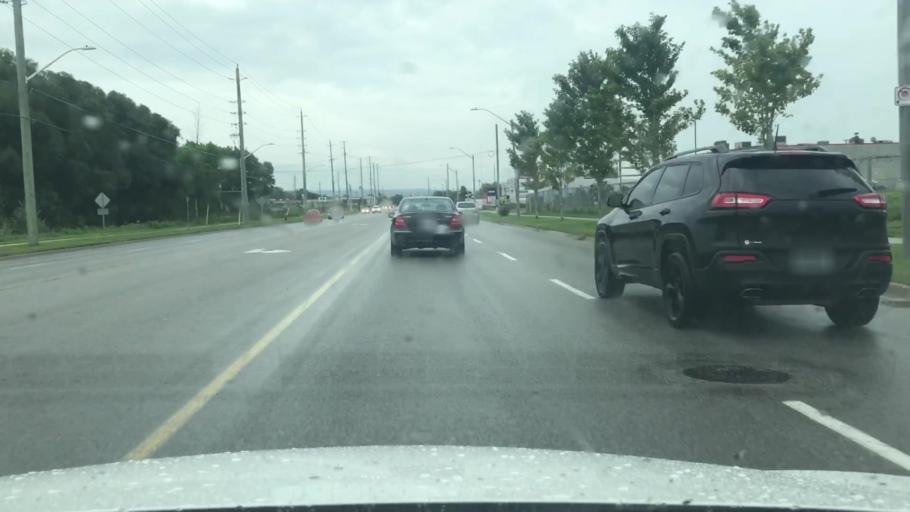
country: CA
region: Ontario
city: Bradford West Gwillimbury
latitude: 44.1198
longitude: -79.5584
